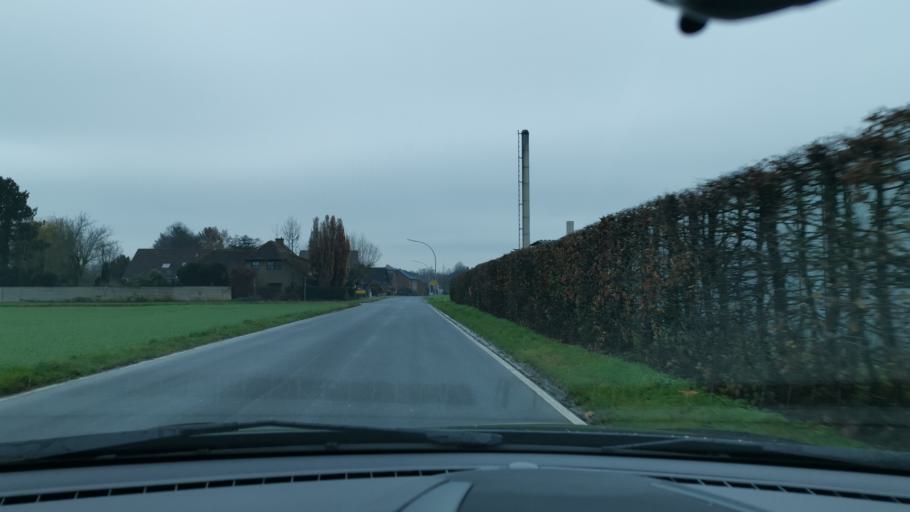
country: DE
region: North Rhine-Westphalia
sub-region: Regierungsbezirk Dusseldorf
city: Juchen
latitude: 51.1174
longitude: 6.5394
